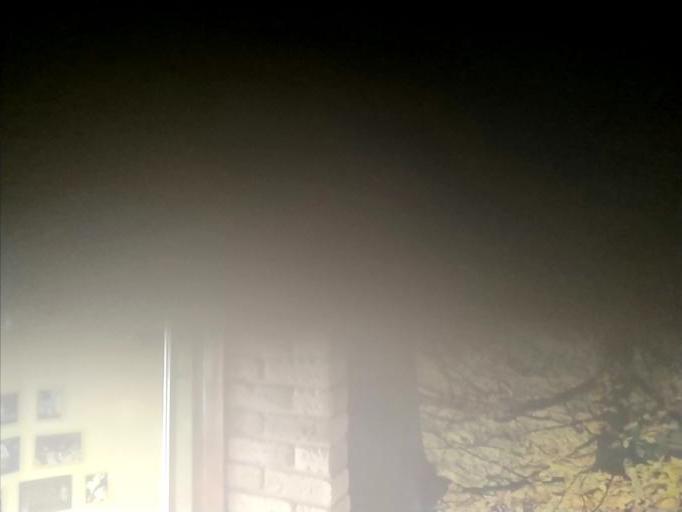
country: RU
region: Kaluga
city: Yukhnov
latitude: 54.6731
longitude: 35.0618
